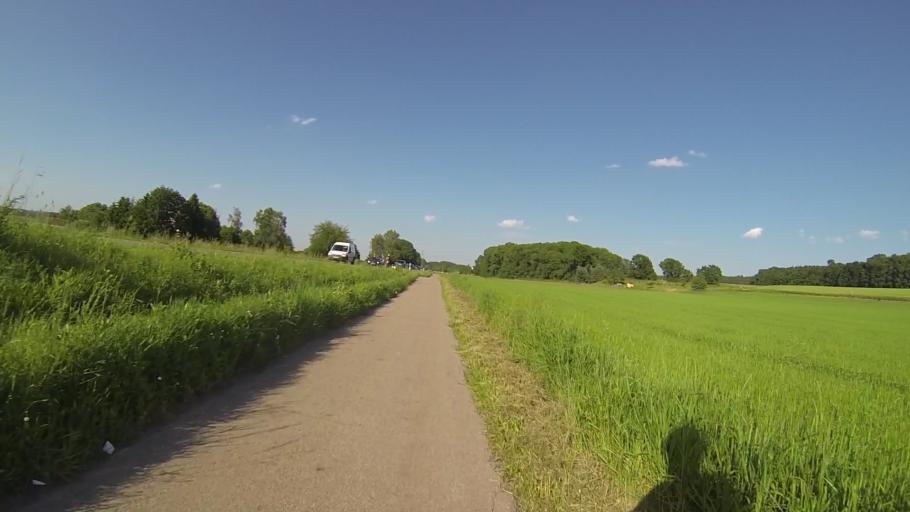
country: DE
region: Baden-Wuerttemberg
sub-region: Tuebingen Region
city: Warthausen
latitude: 48.1431
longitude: 9.8136
